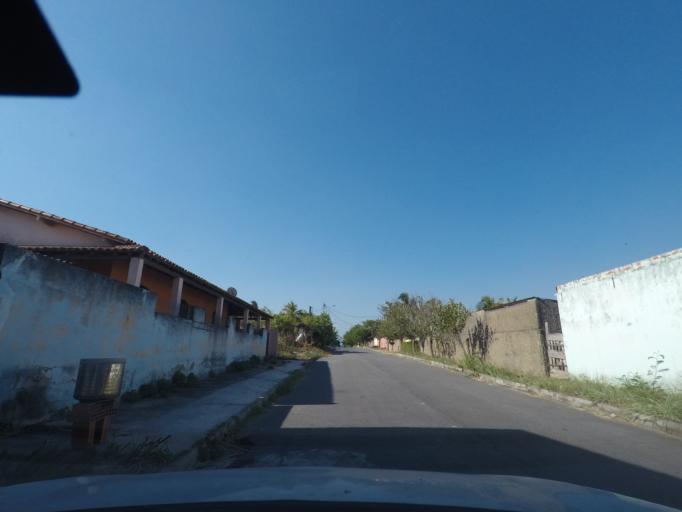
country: BR
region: Rio de Janeiro
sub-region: Marica
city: Marica
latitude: -22.9713
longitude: -42.9199
